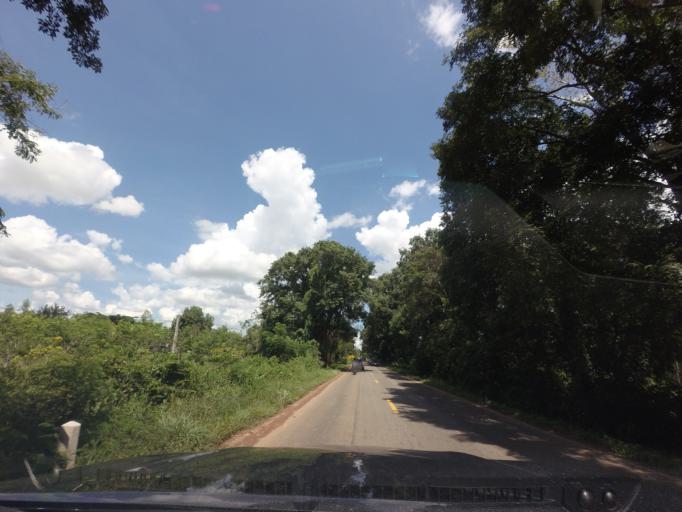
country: TH
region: Changwat Udon Thani
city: Ban Dung
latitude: 17.6642
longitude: 103.1579
